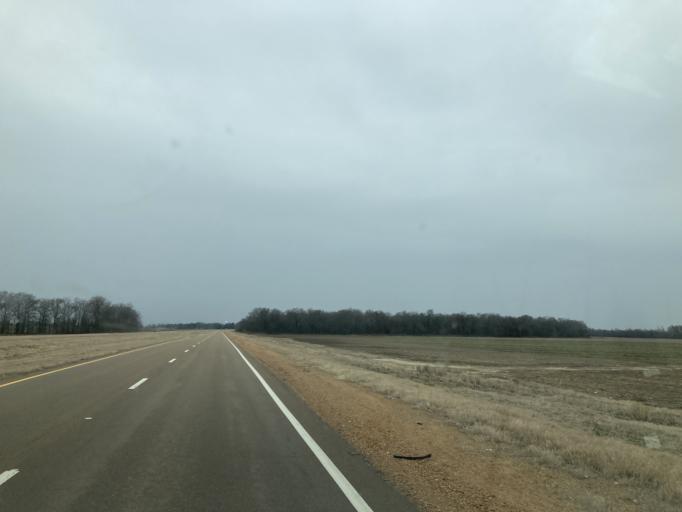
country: US
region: Mississippi
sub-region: Humphreys County
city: Belzoni
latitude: 33.0773
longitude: -90.4786
